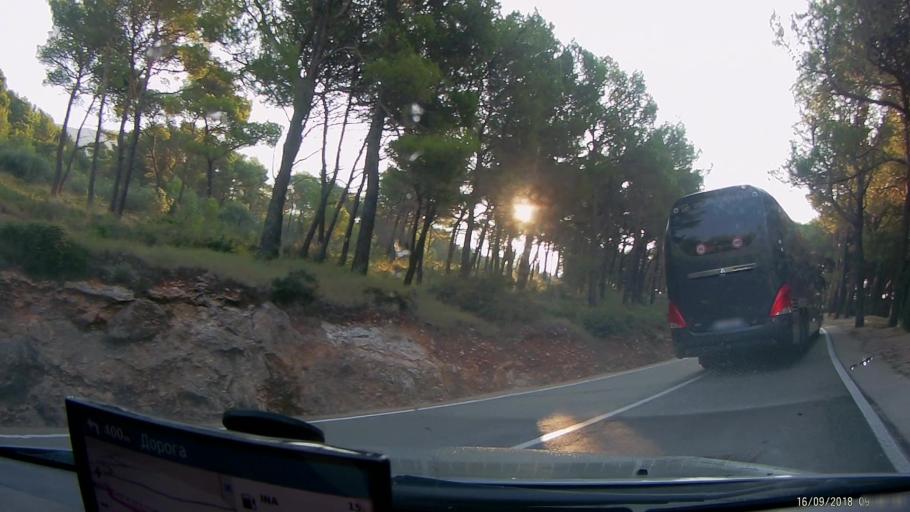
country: HR
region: Splitsko-Dalmatinska
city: Donja Brela
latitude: 43.3726
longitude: 16.9265
